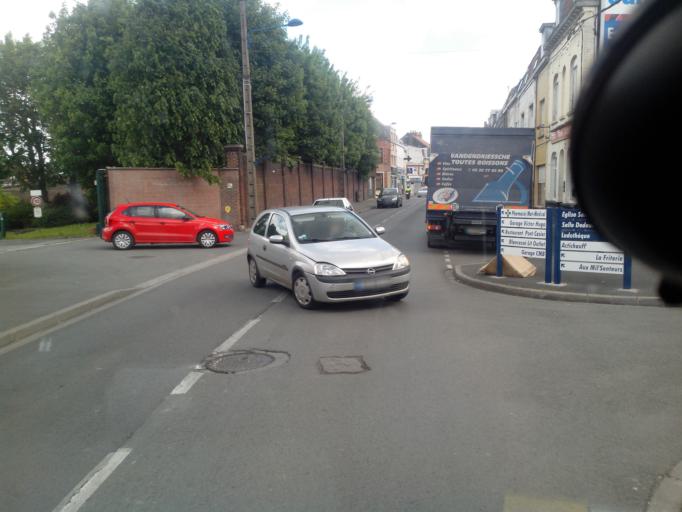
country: FR
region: Nord-Pas-de-Calais
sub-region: Departement du Nord
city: Houplines
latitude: 50.6881
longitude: 2.8998
